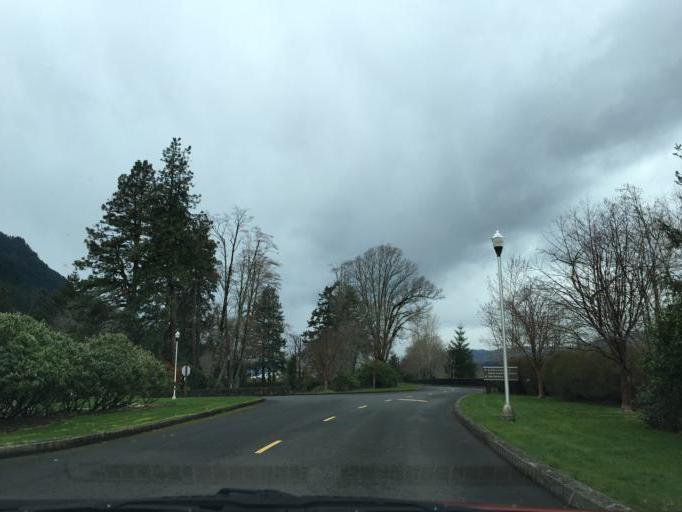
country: US
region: Oregon
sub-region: Hood River County
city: Cascade Locks
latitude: 45.6347
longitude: -121.9560
